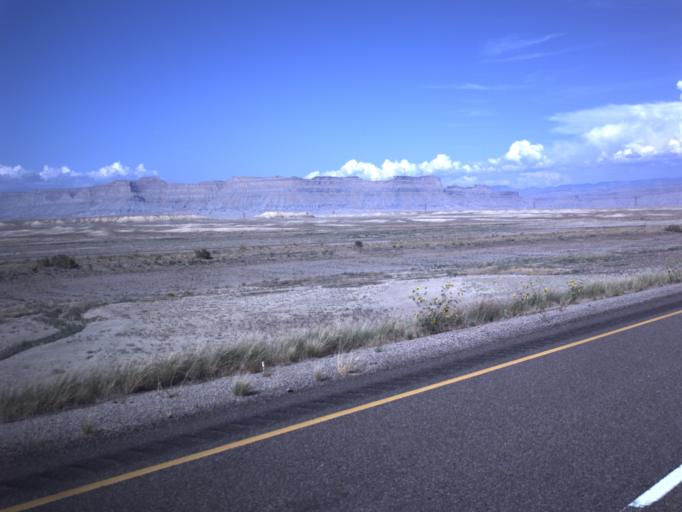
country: US
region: Utah
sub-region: Carbon County
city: East Carbon City
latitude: 38.9582
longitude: -110.2955
